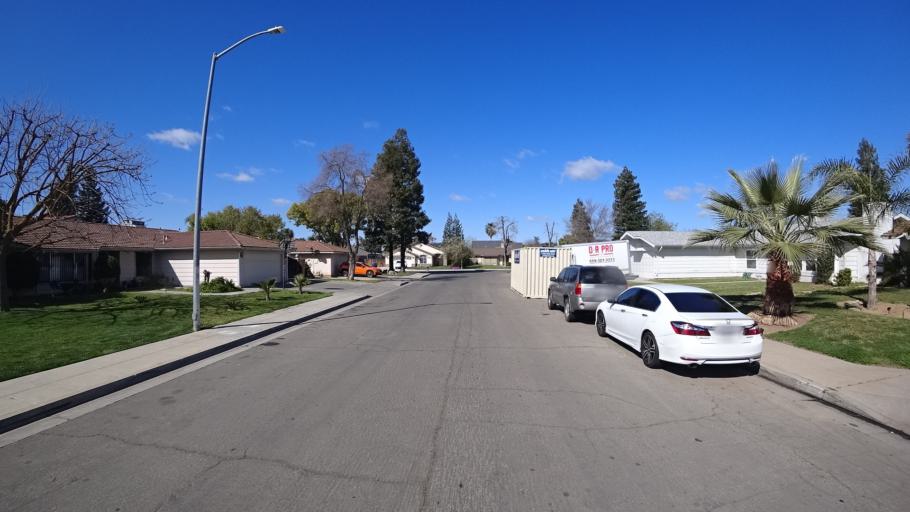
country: US
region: California
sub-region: Fresno County
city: West Park
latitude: 36.7903
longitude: -119.8862
